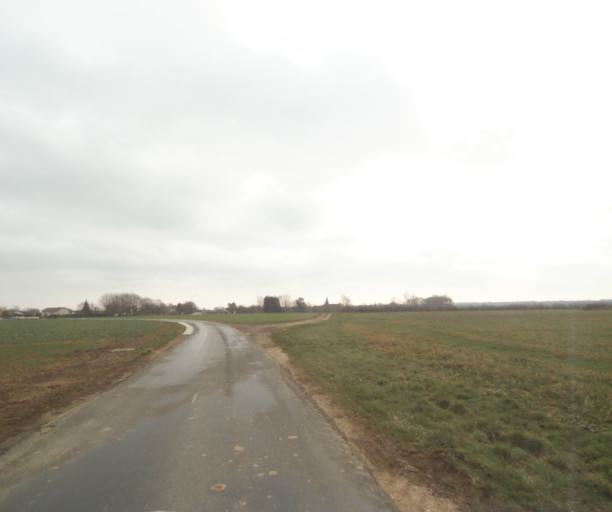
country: FR
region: Champagne-Ardenne
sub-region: Departement de la Haute-Marne
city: Villiers-en-Lieu
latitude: 48.6833
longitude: 4.8275
